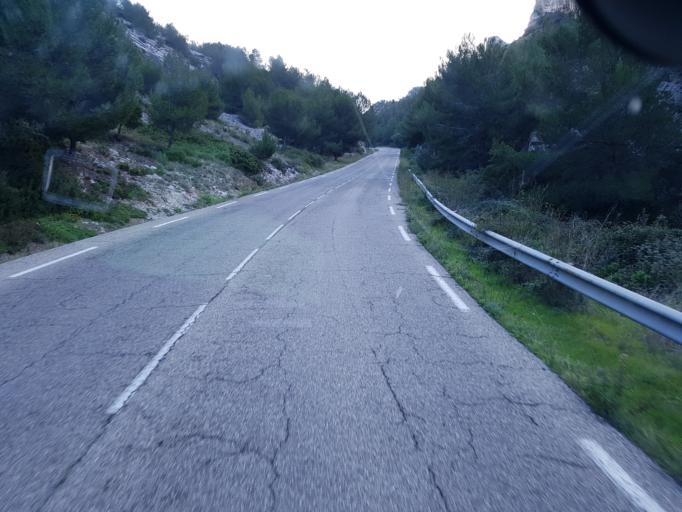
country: FR
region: Provence-Alpes-Cote d'Azur
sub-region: Departement des Bouches-du-Rhone
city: Le Rove
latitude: 43.3499
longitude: 5.2432
